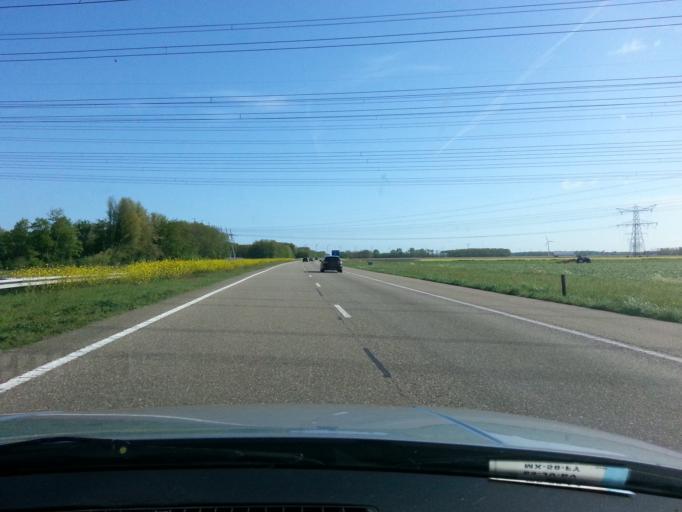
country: NL
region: Flevoland
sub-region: Gemeente Lelystad
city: Lelystad
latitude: 52.5701
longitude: 5.5356
